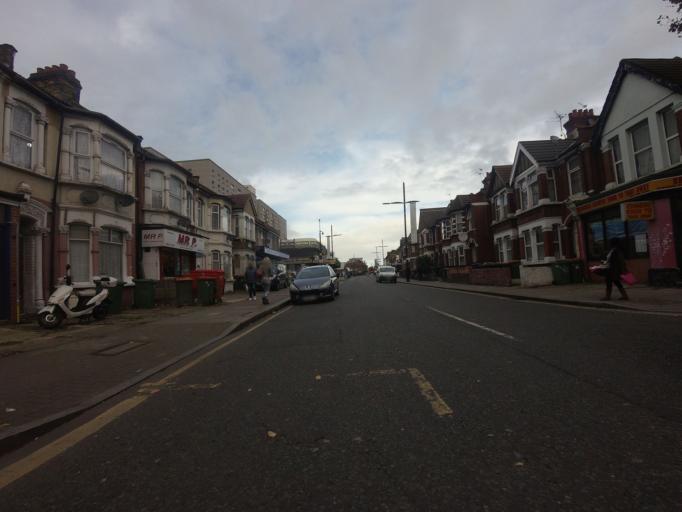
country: GB
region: England
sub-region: Greater London
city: East Ham
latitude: 51.5335
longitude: 0.0363
